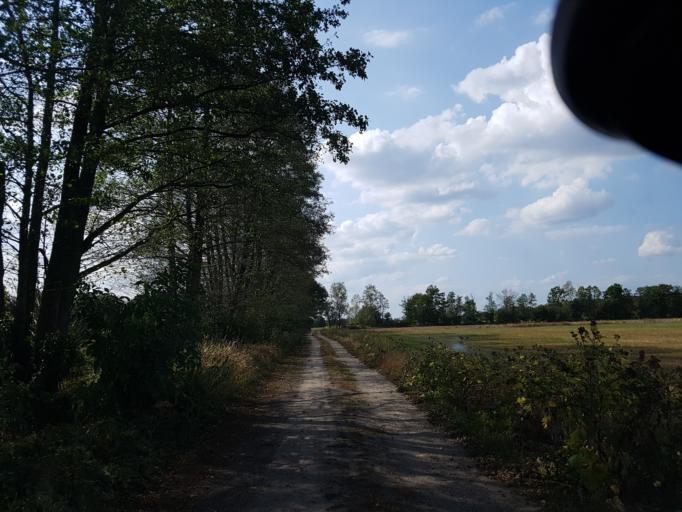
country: DE
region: Brandenburg
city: Calau
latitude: 51.7709
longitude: 13.9678
